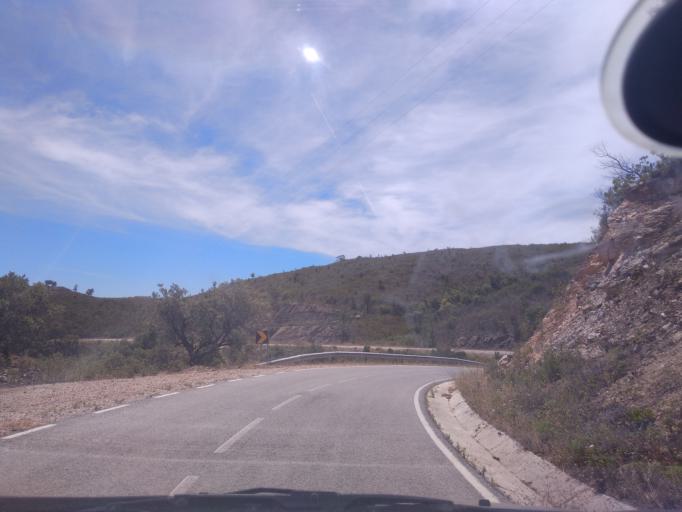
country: PT
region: Faro
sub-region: Sao Bras de Alportel
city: Sao Bras de Alportel
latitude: 37.2036
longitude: -7.8098
